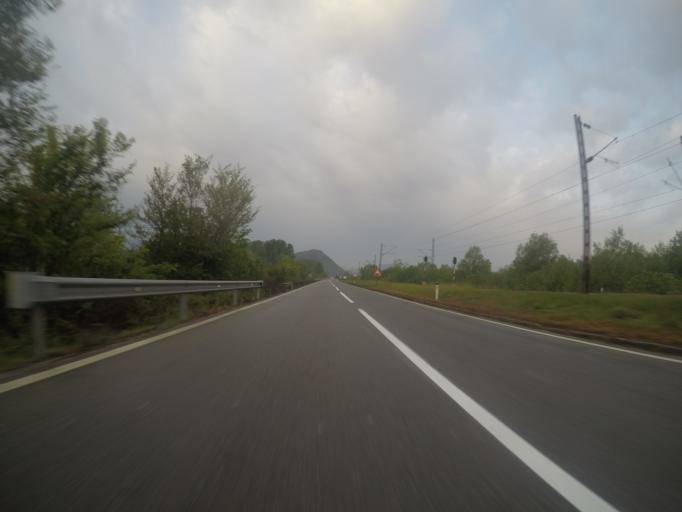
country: ME
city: Mojanovici
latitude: 42.2938
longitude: 19.1563
